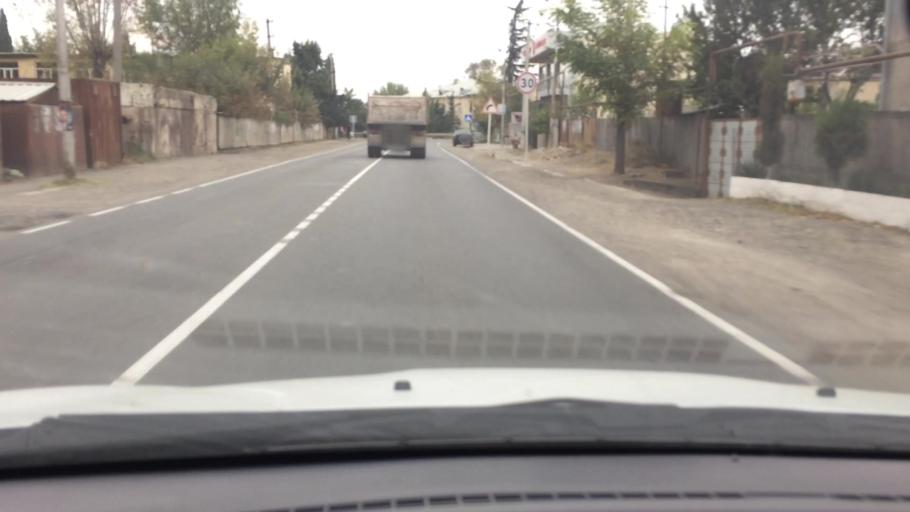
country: GE
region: Kvemo Kartli
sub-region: Marneuli
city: Marneuli
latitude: 41.4844
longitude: 44.8010
